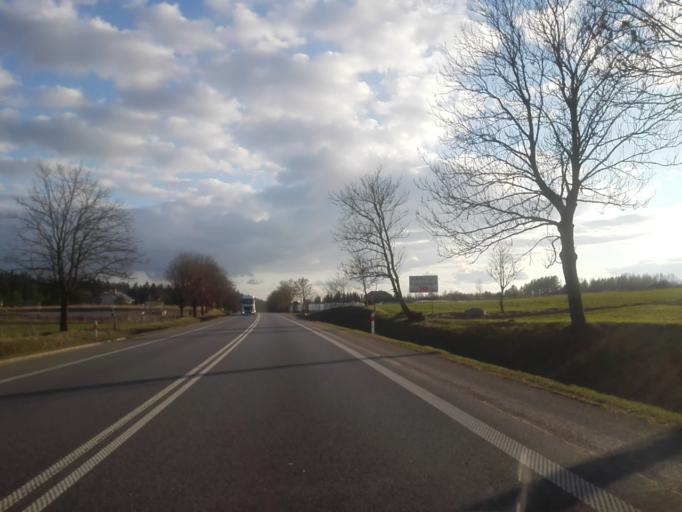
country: PL
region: Podlasie
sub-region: Suwalki
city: Suwalki
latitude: 54.1638
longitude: 22.9822
